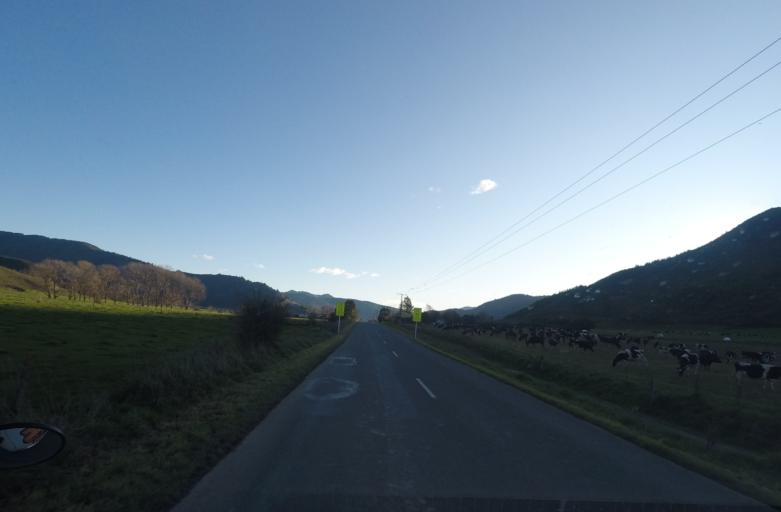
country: NZ
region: Marlborough
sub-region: Marlborough District
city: Picton
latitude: -41.2900
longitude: 173.8834
